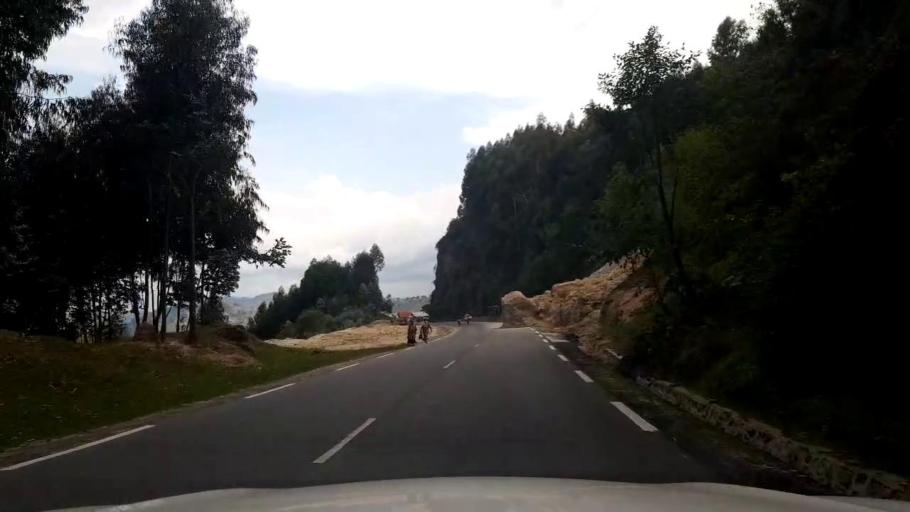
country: RW
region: Northern Province
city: Musanze
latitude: -1.6702
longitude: 29.5147
